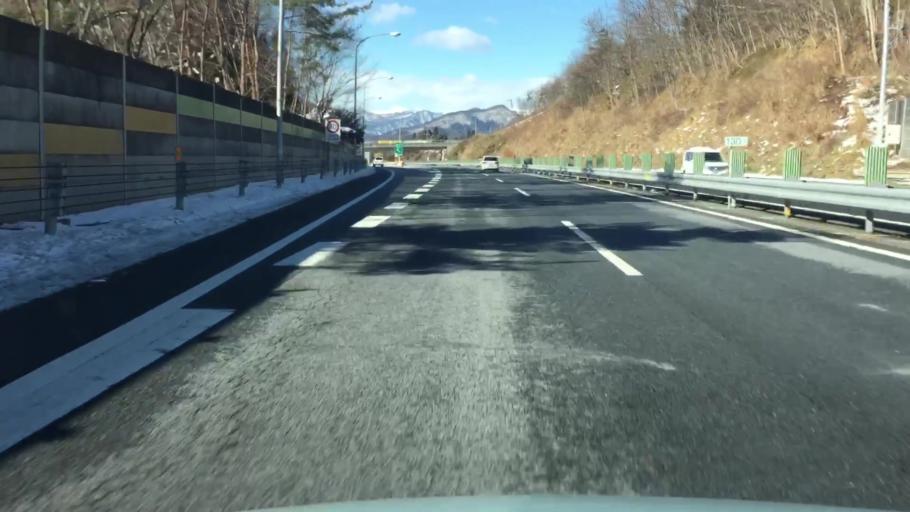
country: JP
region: Gunma
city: Numata
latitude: 36.6754
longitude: 139.0262
